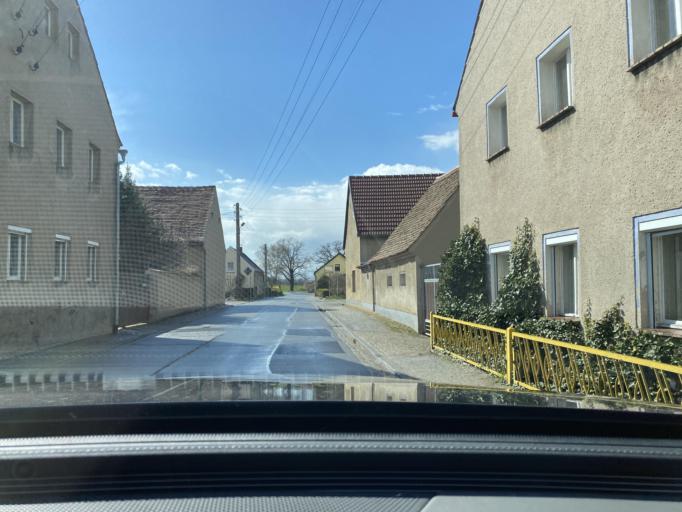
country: DE
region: Saxony
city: Radibor
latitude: 51.2440
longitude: 14.3951
